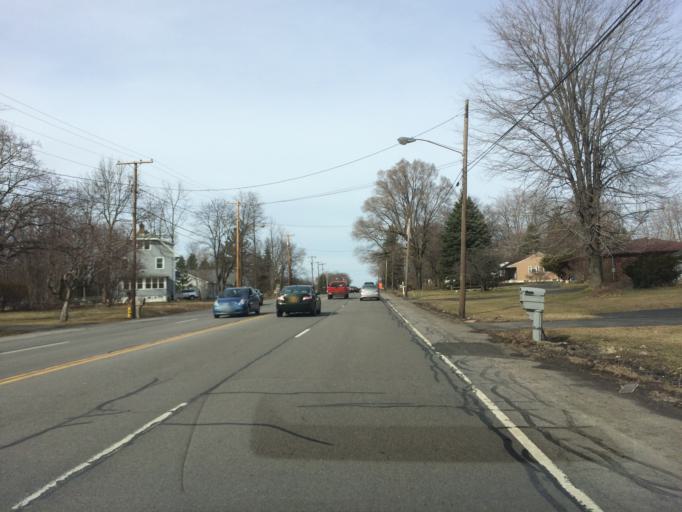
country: US
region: New York
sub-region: Monroe County
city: Rochester
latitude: 43.1055
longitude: -77.6271
